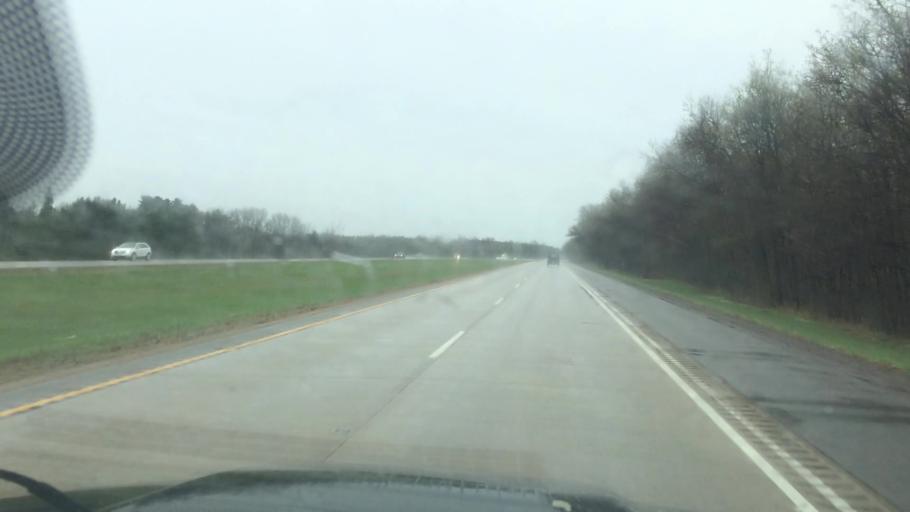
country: US
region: Wisconsin
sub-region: Portage County
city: Stevens Point
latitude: 44.6511
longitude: -89.6391
